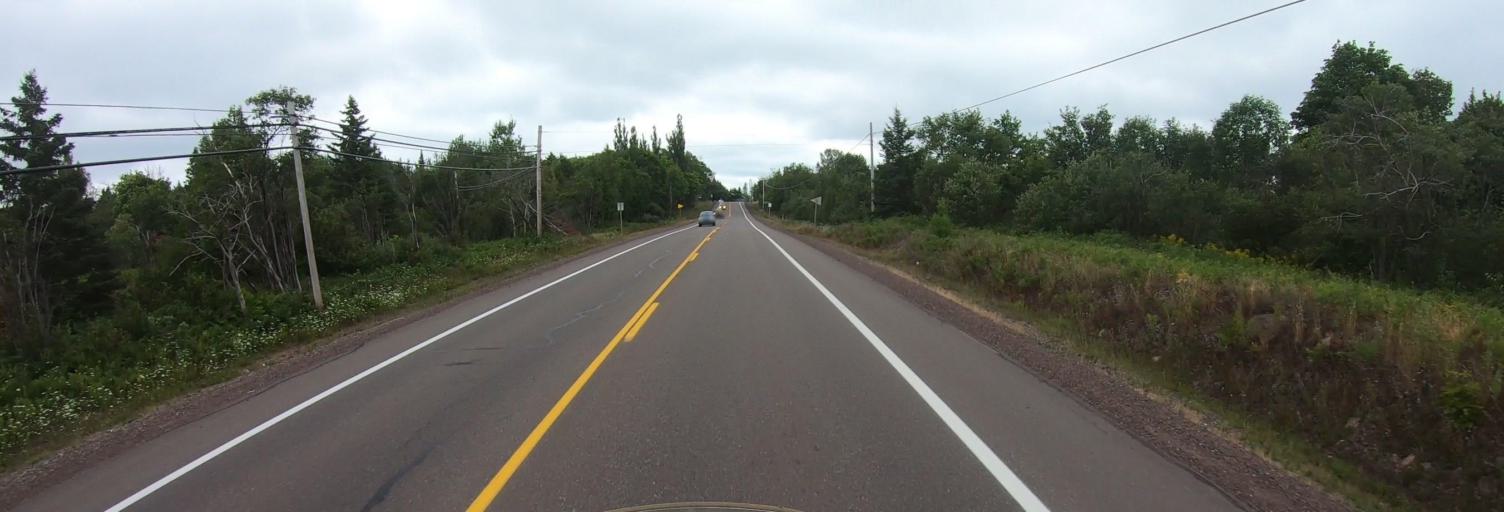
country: US
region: Michigan
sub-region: Houghton County
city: Laurium
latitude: 47.2779
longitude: -88.4141
